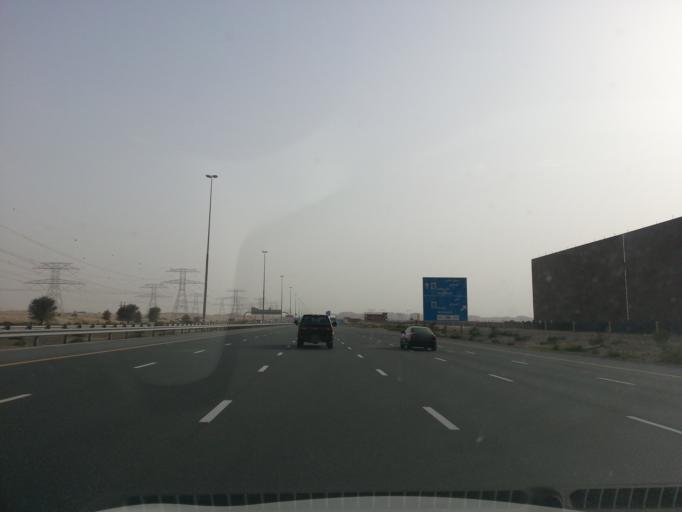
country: AE
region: Dubai
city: Dubai
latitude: 25.0164
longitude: 55.2746
